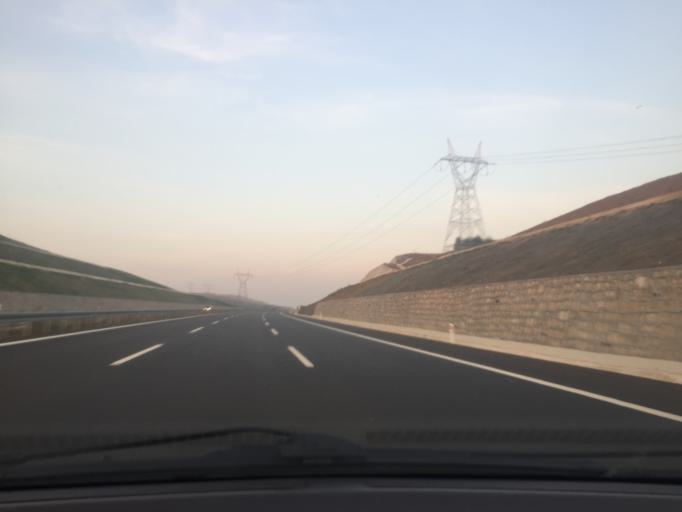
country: TR
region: Bursa
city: Mahmudiye
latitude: 40.2744
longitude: 28.5553
